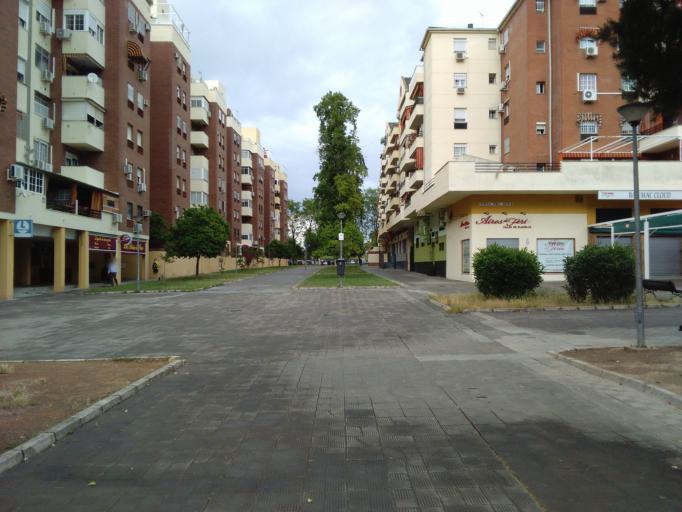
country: ES
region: Andalusia
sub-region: Provincia de Sevilla
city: Sevilla
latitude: 37.4021
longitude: -5.9381
